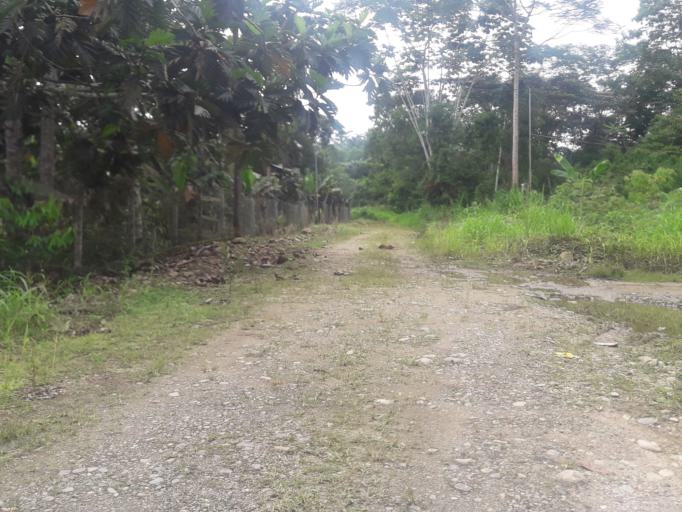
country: EC
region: Napo
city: Tena
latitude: -0.9744
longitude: -77.8470
